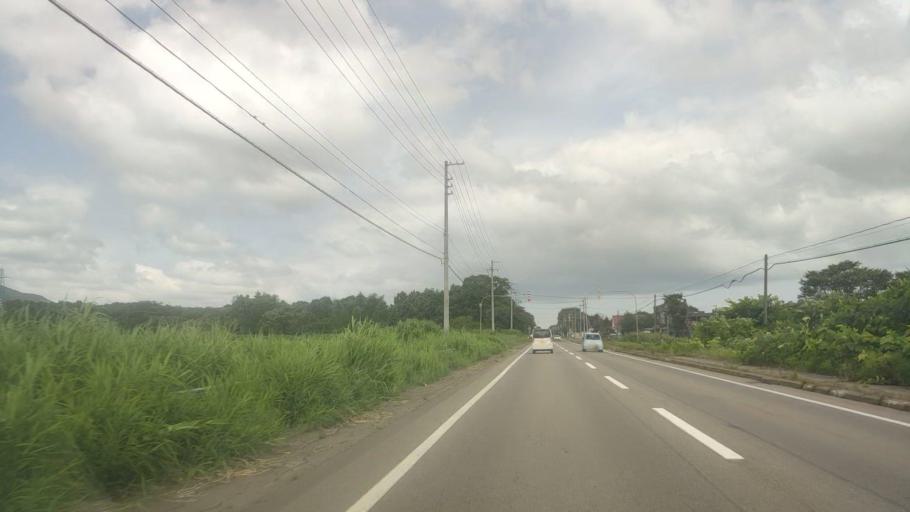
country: JP
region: Hokkaido
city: Nanae
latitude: 42.0332
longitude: 140.6087
